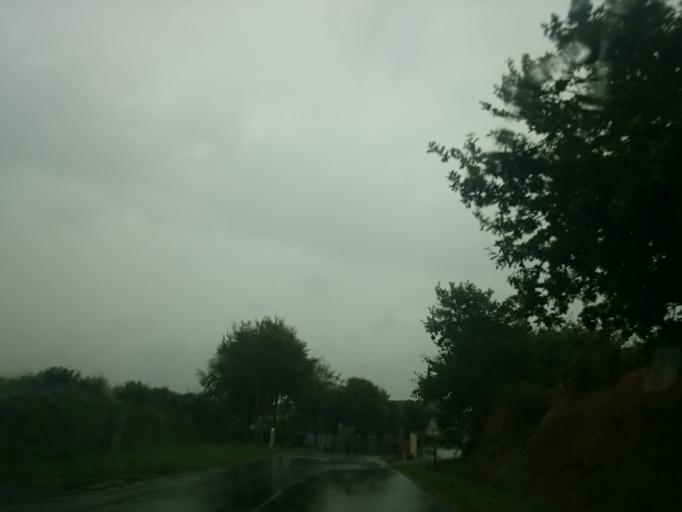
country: FR
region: Brittany
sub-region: Departement du Finistere
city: Plouvien
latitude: 48.5360
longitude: -4.4274
